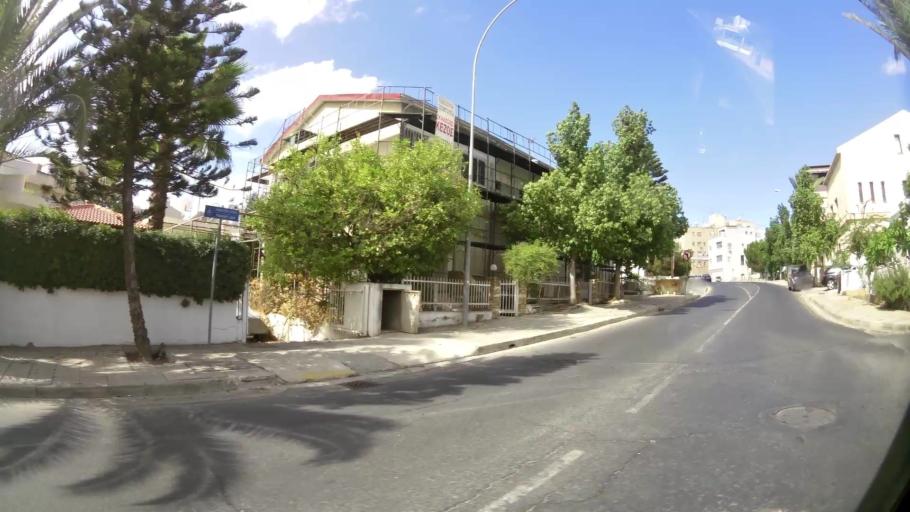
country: CY
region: Lefkosia
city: Nicosia
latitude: 35.1479
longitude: 33.3612
